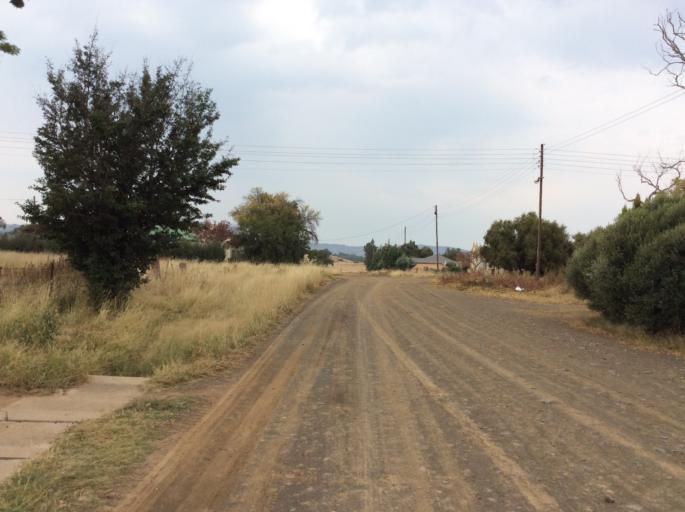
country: LS
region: Mafeteng
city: Mafeteng
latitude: -29.9888
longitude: 27.0148
